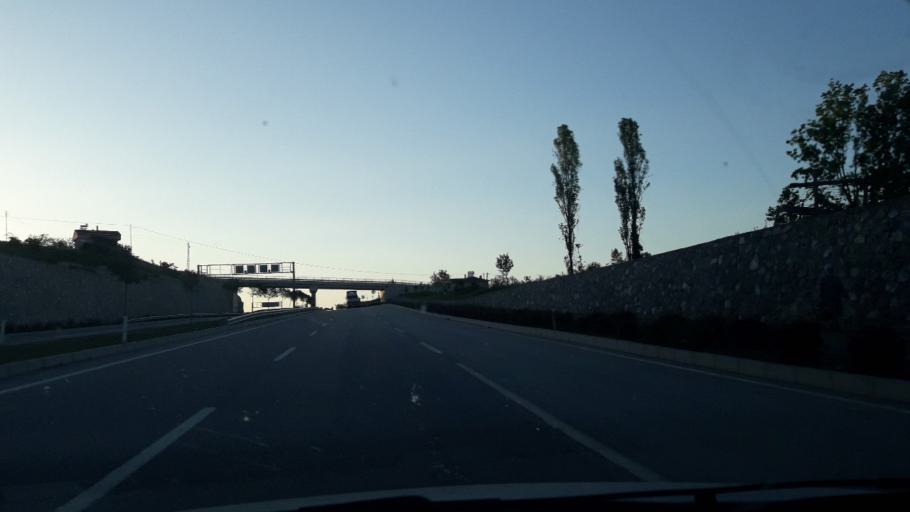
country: TR
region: Sinop
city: Gerze
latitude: 41.7936
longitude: 35.1875
